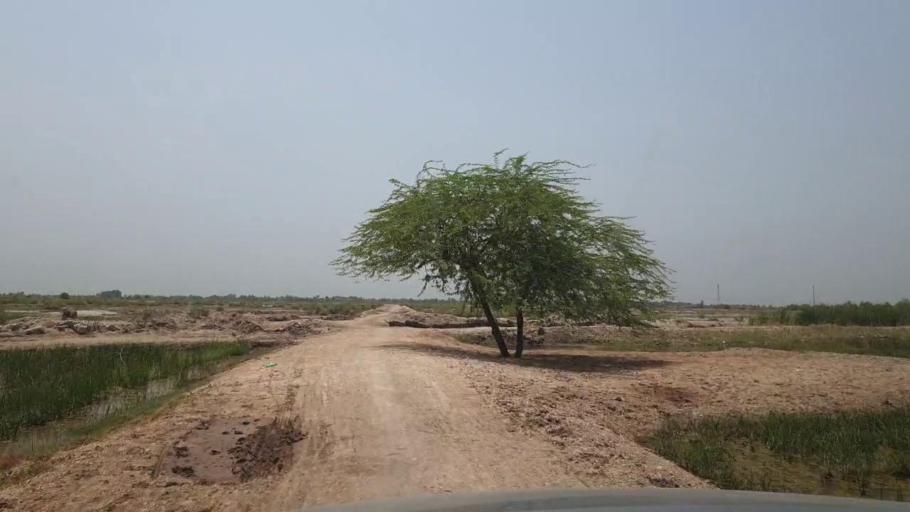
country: PK
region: Sindh
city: Garhi Yasin
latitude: 27.8607
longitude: 68.4794
